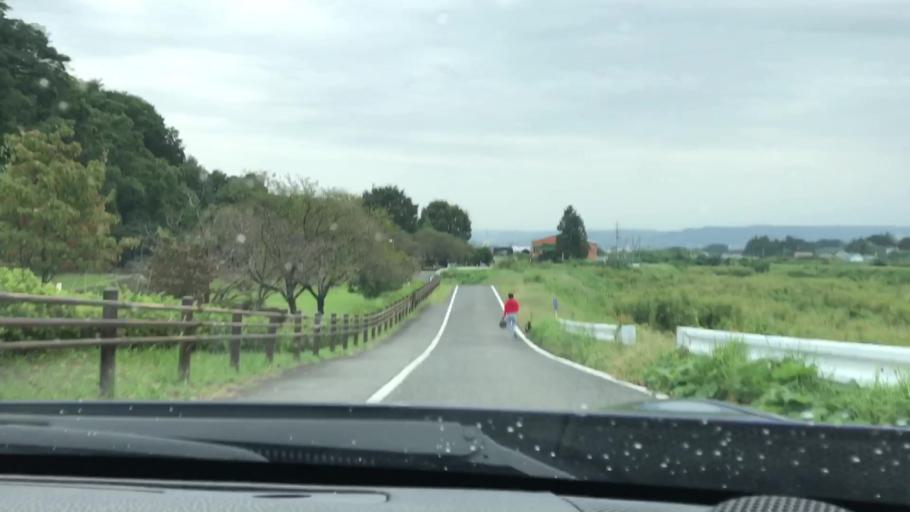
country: JP
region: Gunma
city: Kanekomachi
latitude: 36.3961
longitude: 138.9506
